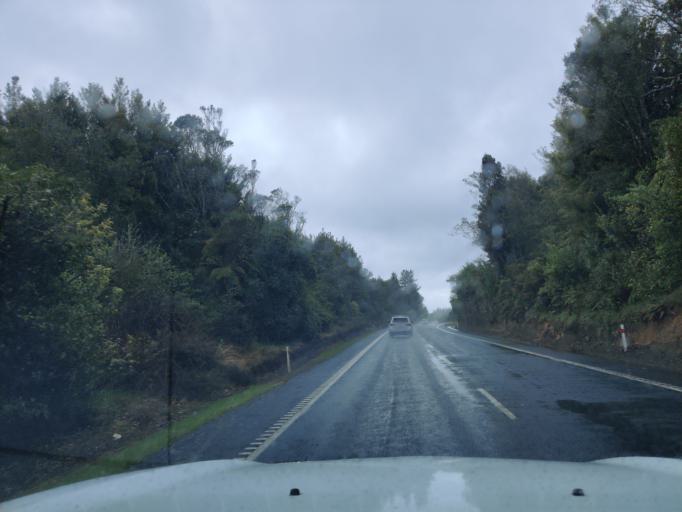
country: NZ
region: Bay of Plenty
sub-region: Rotorua District
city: Rotorua
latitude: -38.0582
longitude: 176.0911
